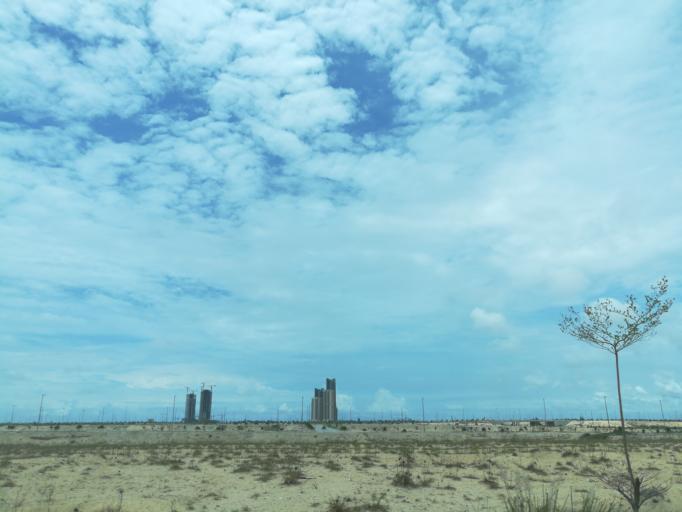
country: NG
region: Lagos
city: Ikoyi
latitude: 6.4139
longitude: 3.4252
